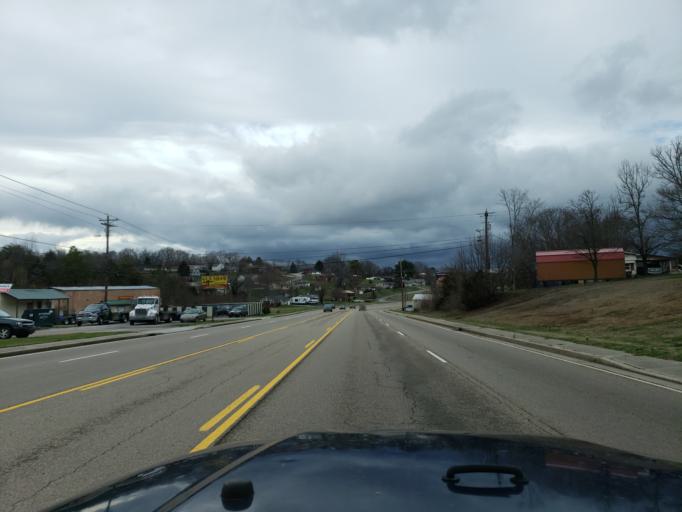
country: US
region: Tennessee
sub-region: Jefferson County
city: Jefferson City
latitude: 36.0959
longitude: -83.4792
